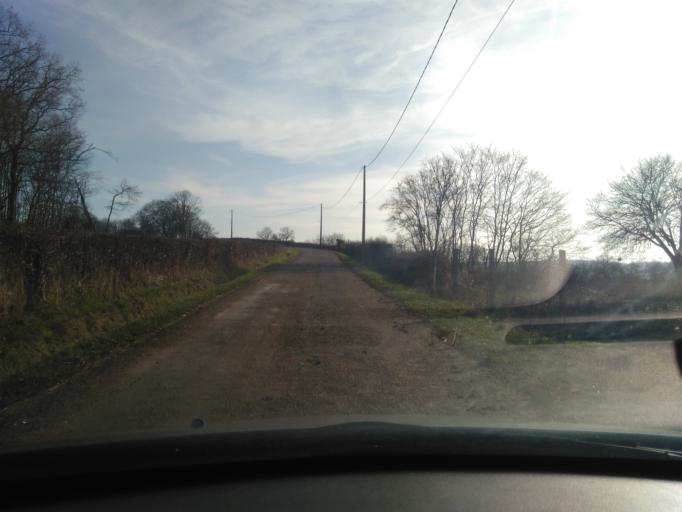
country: FR
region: Bourgogne
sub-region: Departement de la Nievre
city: Saint-Parize-le-Chatel
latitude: 46.8342
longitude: 3.2374
